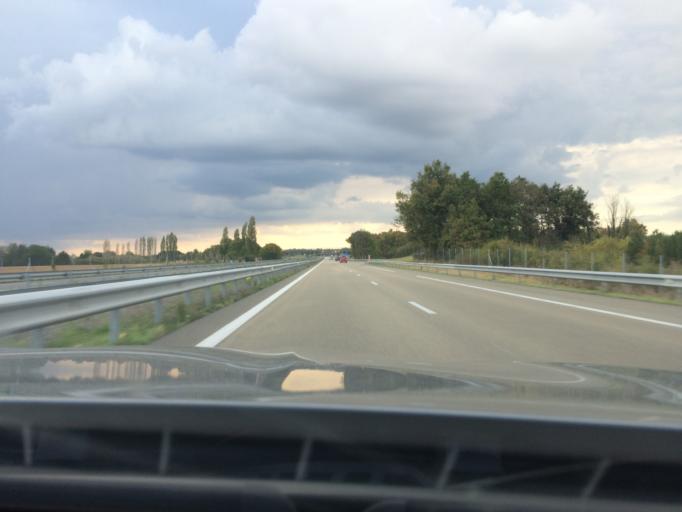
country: FR
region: Ile-de-France
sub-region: Departement de Seine-et-Marne
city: Egreville
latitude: 48.1791
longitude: 2.8456
